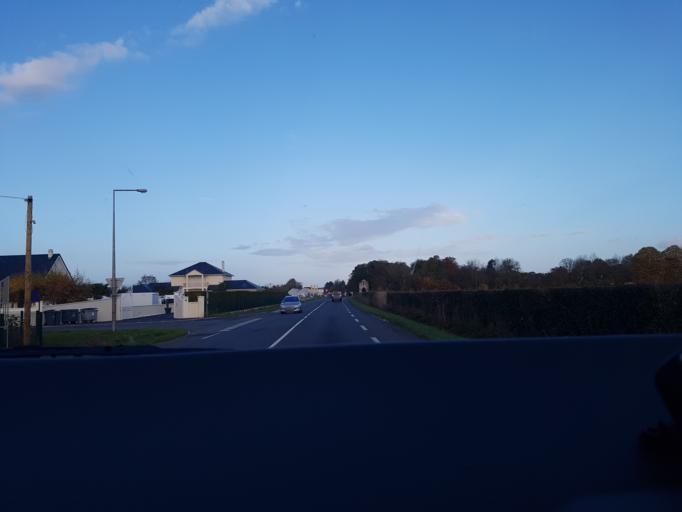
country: FR
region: Lower Normandy
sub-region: Departement du Calvados
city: Sannerville
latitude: 49.1752
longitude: -0.2341
